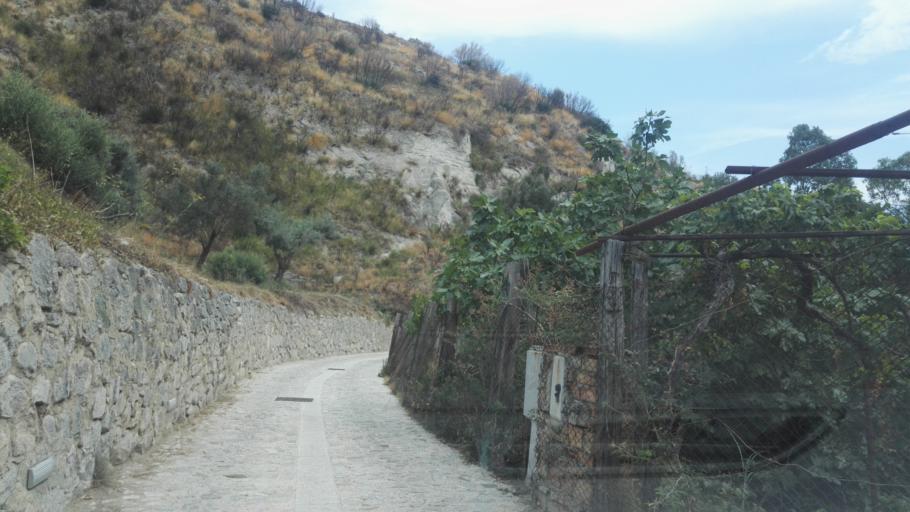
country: IT
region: Calabria
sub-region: Provincia di Reggio Calabria
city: Roccella Ionica
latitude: 38.3274
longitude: 16.4095
